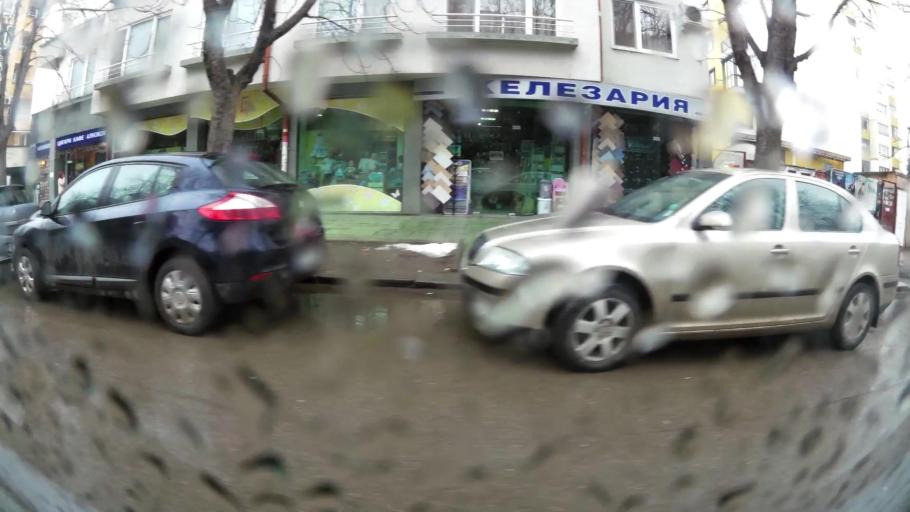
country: BG
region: Sofia-Capital
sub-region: Stolichna Obshtina
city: Sofia
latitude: 42.6725
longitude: 23.2995
